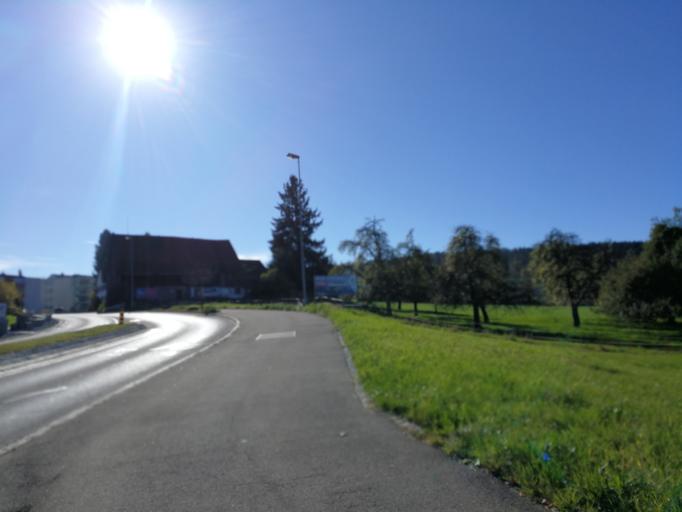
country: CH
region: Zurich
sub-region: Bezirk Meilen
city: Oetwil am See
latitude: 47.2751
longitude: 8.7228
